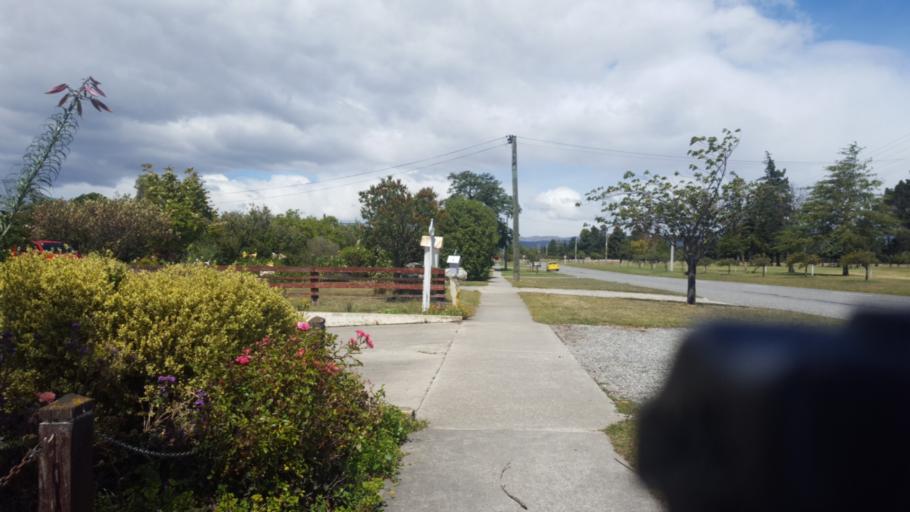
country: NZ
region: Otago
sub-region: Queenstown-Lakes District
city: Wanaka
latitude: -45.1934
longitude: 169.3252
